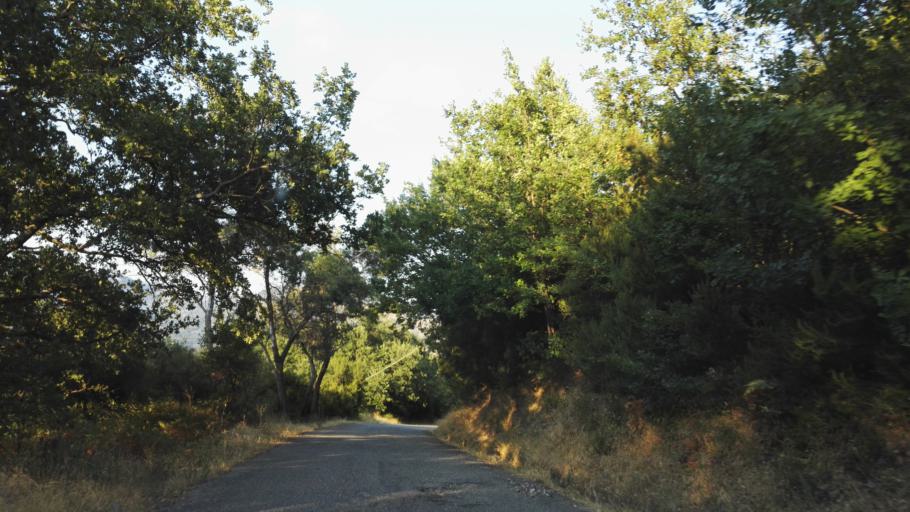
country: IT
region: Calabria
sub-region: Provincia di Reggio Calabria
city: Caulonia
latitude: 38.4060
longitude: 16.3670
